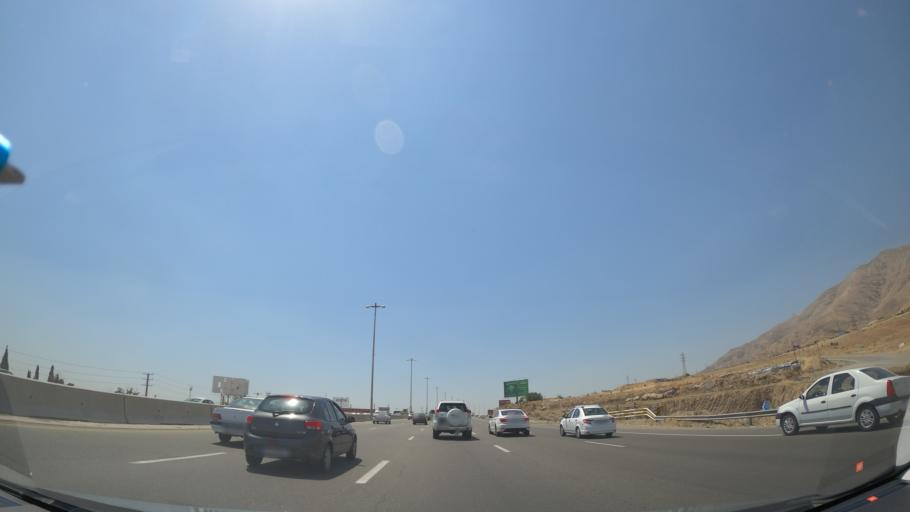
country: IR
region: Tehran
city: Shahr-e Qods
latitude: 35.7454
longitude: 51.0910
